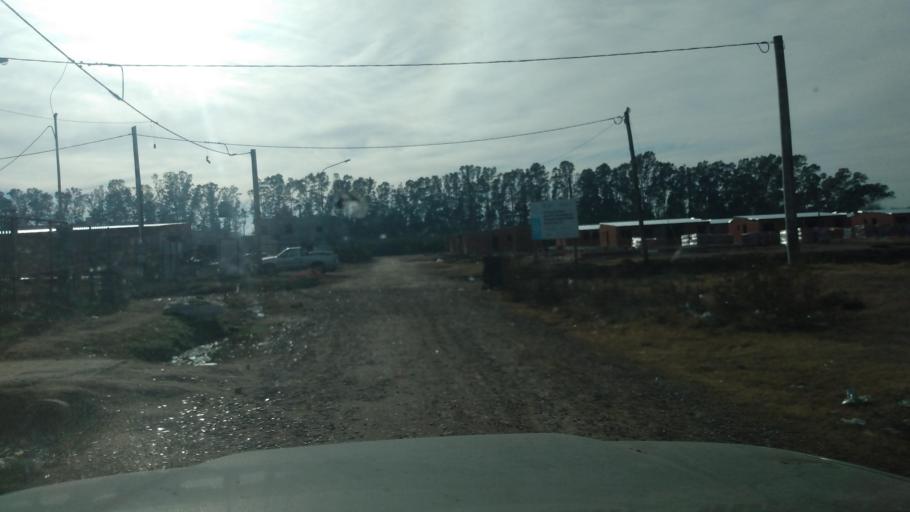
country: AR
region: Buenos Aires
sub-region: Partido de Lujan
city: Lujan
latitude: -34.5394
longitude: -59.1139
